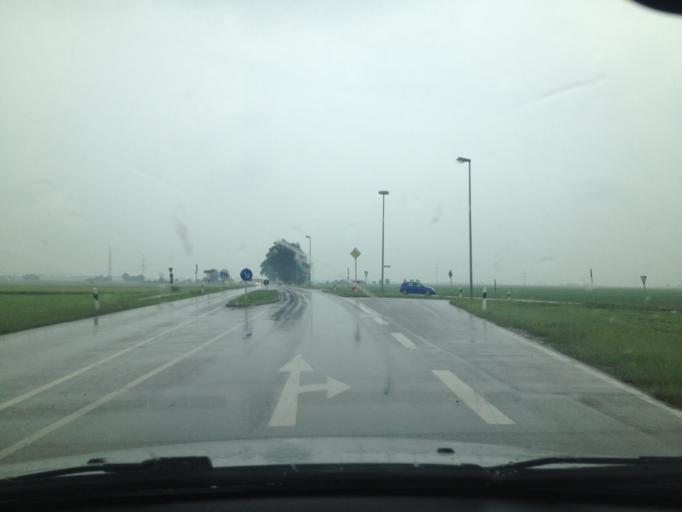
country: DE
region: Bavaria
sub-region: Swabia
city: Schwabmunchen
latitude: 48.1734
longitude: 10.7699
